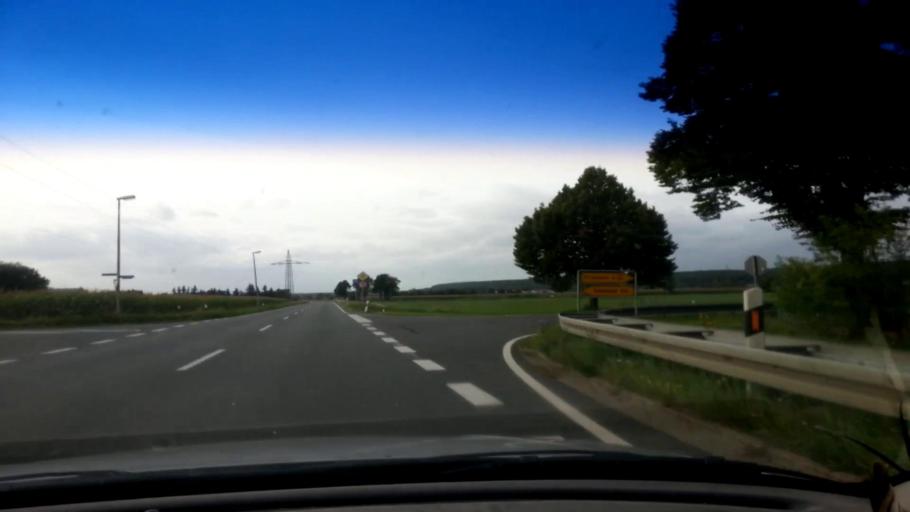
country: DE
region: Bavaria
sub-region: Upper Franconia
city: Hirschaid
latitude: 49.8257
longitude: 10.9949
